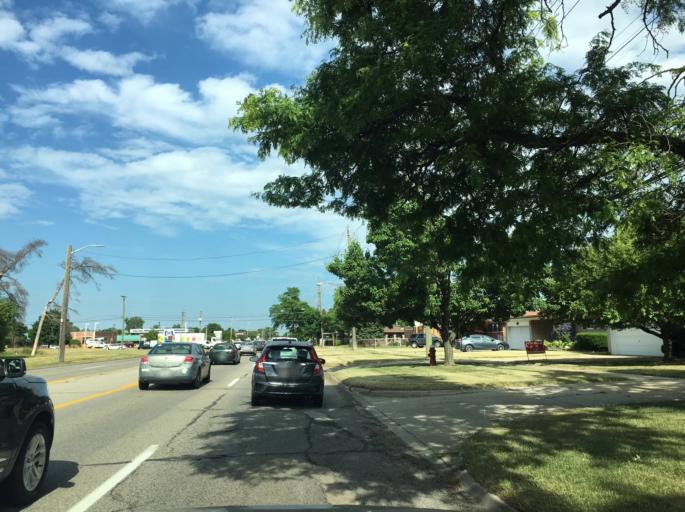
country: US
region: Michigan
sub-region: Macomb County
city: Fraser
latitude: 42.5376
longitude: -82.9958
